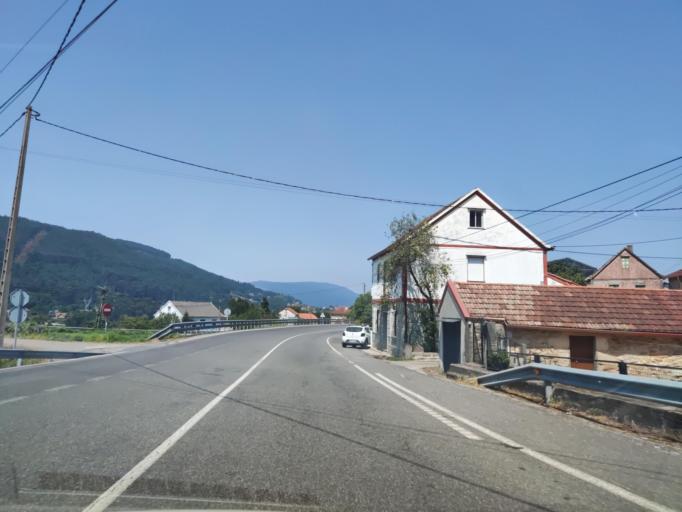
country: ES
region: Galicia
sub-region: Provincia de Pontevedra
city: Redondela
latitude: 42.2625
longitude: -8.6037
